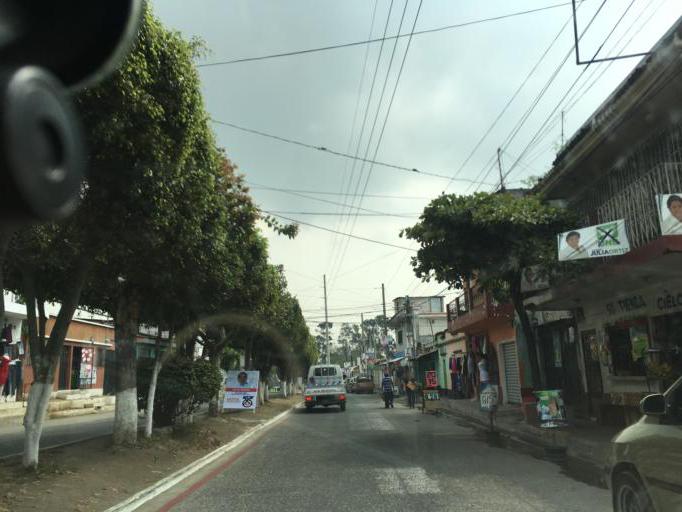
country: GT
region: Guatemala
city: Petapa
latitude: 14.5040
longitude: -90.5605
